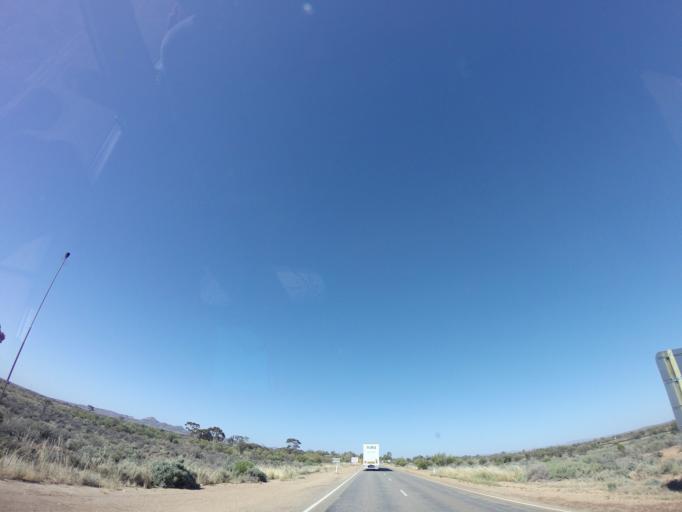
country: AU
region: South Australia
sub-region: Peterborough
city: Peterborough
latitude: -32.6133
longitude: 139.5173
